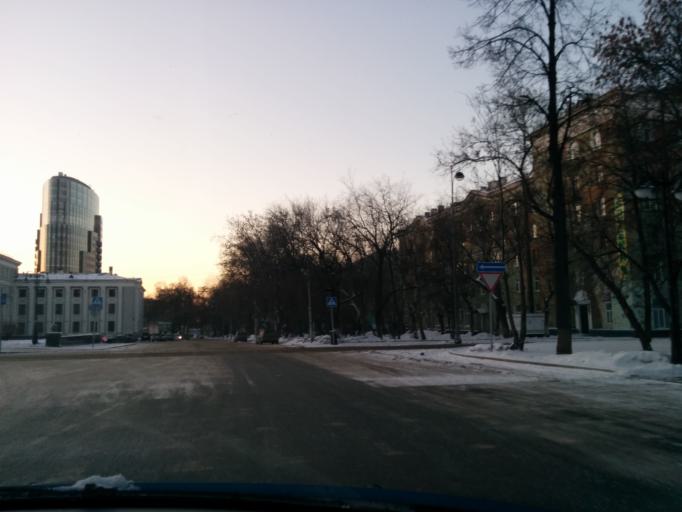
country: RU
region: Perm
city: Perm
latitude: 57.9914
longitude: 56.2528
